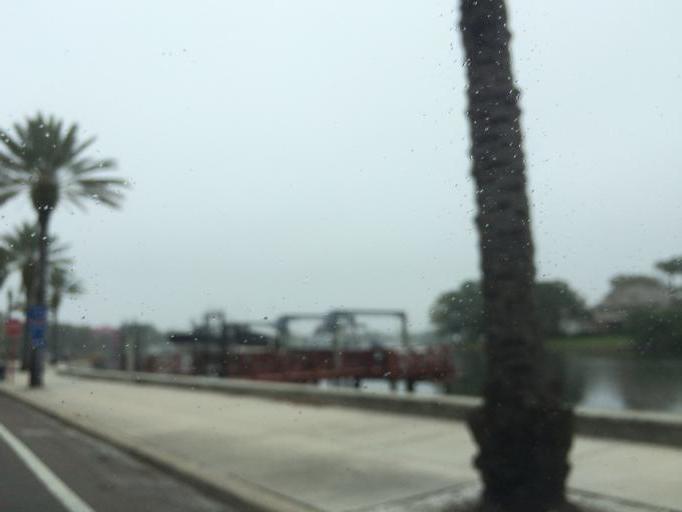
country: US
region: Florida
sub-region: Pinellas County
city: Saint Petersburg
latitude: 27.7924
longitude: -82.6283
